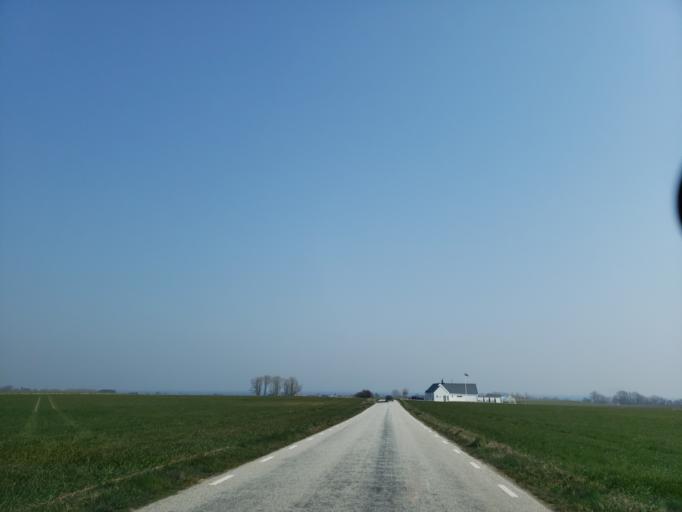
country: SE
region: Skane
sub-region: Simrishamns Kommun
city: Simrishamn
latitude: 55.5109
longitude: 14.3234
